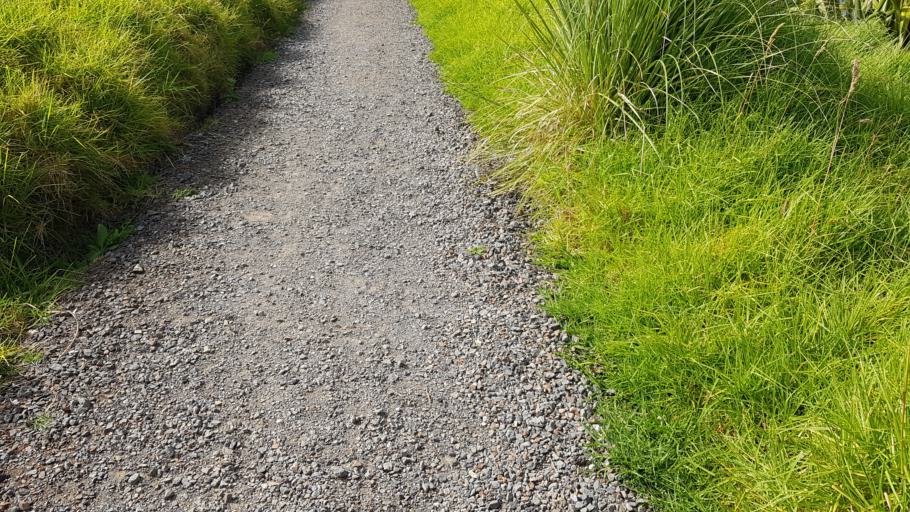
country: NZ
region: Auckland
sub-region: Auckland
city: Rothesay Bay
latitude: -36.6694
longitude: 174.7464
